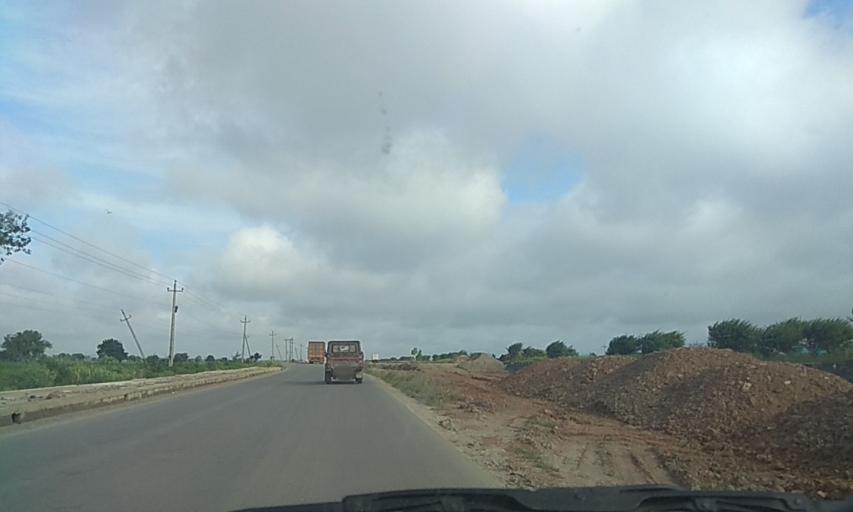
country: IN
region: Karnataka
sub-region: Haveri
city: Savanur
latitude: 14.8854
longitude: 75.3048
